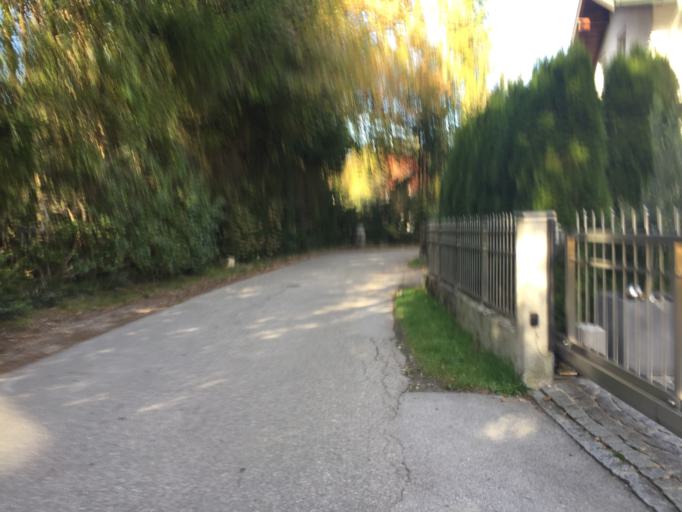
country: AT
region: Salzburg
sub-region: Politischer Bezirk Salzburg-Umgebung
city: Grodig
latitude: 47.7514
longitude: 12.9954
